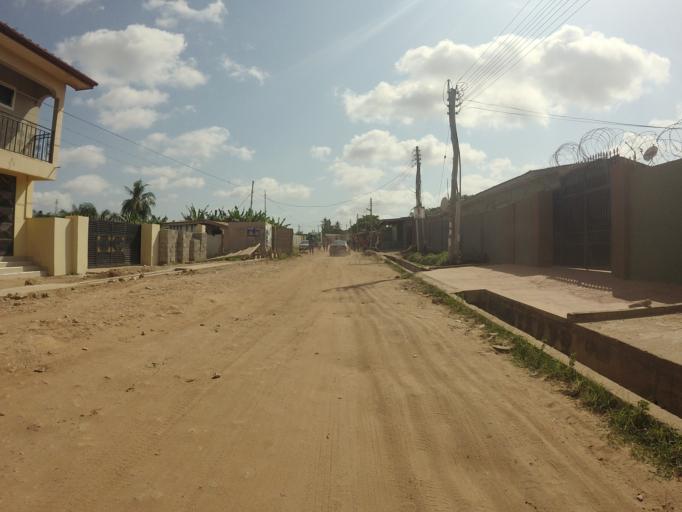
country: GH
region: Greater Accra
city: Dome
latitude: 5.6179
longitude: -0.2421
